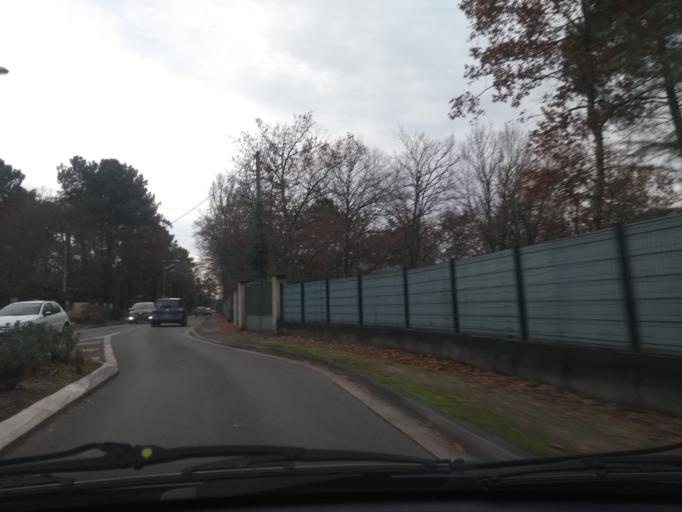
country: FR
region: Aquitaine
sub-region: Departement de la Gironde
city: Gradignan
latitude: 44.7507
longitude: -0.6165
